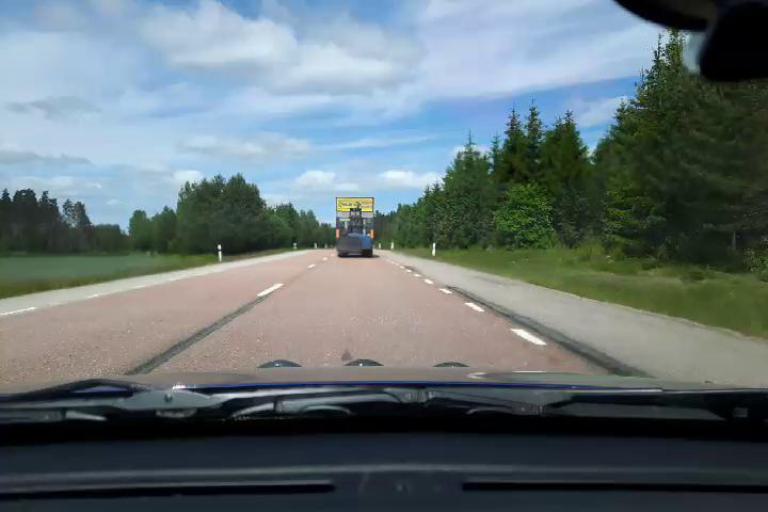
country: SE
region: Uppsala
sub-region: Osthammars Kommun
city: Bjorklinge
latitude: 60.1579
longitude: 17.4911
